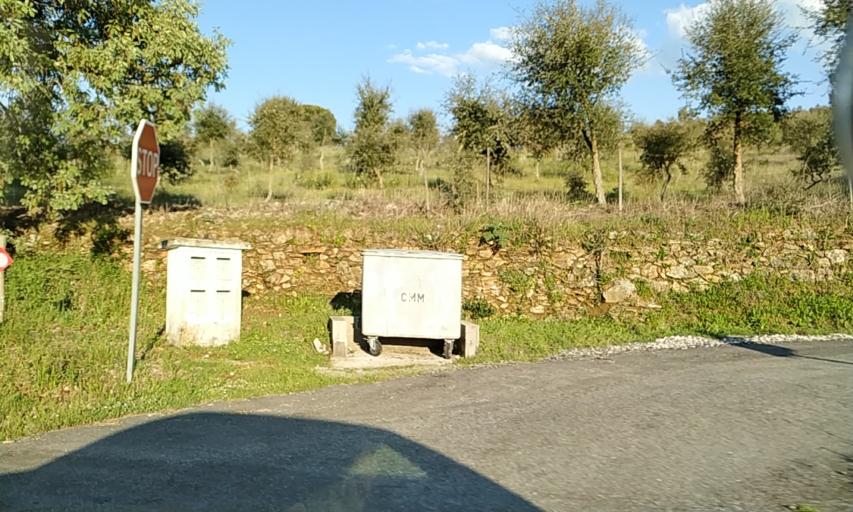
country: PT
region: Portalegre
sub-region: Marvao
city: Marvao
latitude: 39.3654
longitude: -7.3912
